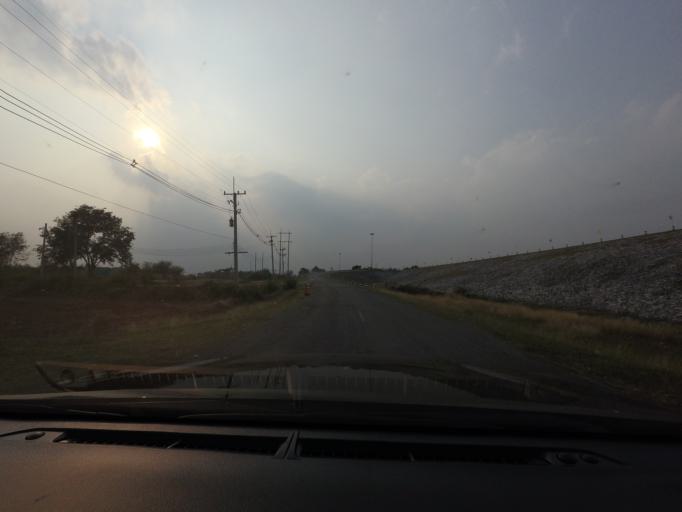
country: TH
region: Sara Buri
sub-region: Amphoe Wang Muang
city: Wang Muang
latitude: 14.8611
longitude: 101.0683
